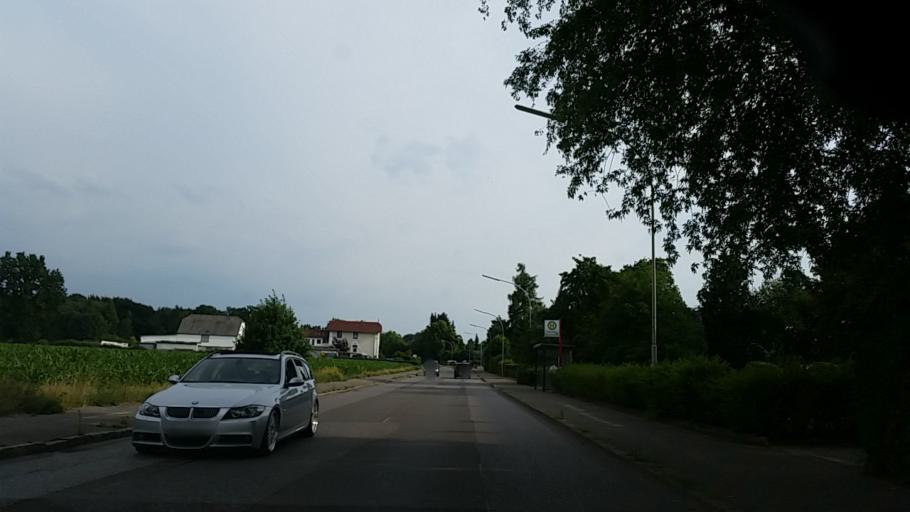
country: DE
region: Schleswig-Holstein
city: Halstenbek
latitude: 53.5964
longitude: 9.8221
